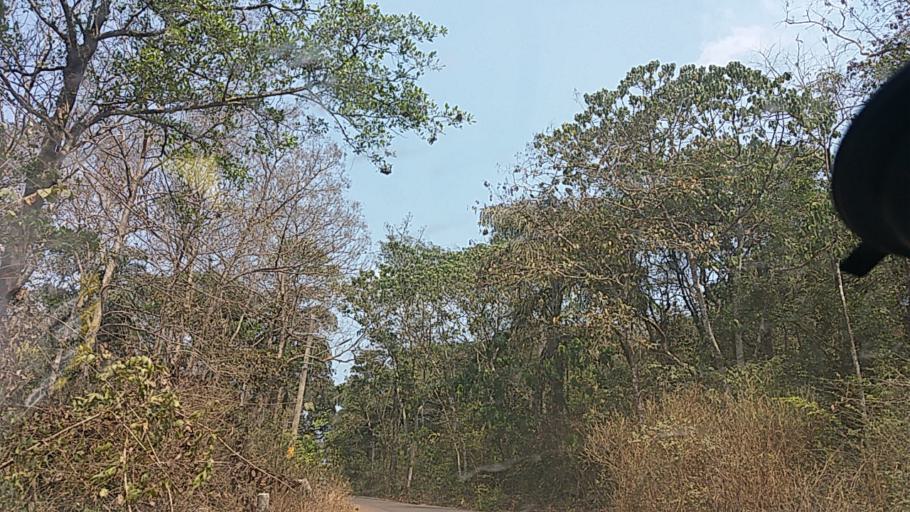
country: IN
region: Goa
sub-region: South Goa
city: Sancoale
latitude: 15.3750
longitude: 73.9136
